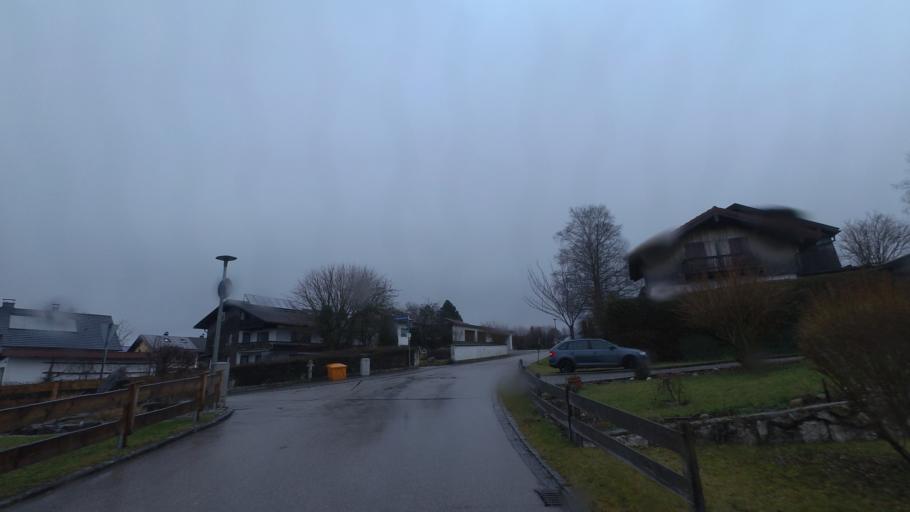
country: DE
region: Bavaria
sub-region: Upper Bavaria
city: Nussdorf
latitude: 47.9230
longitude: 12.6473
